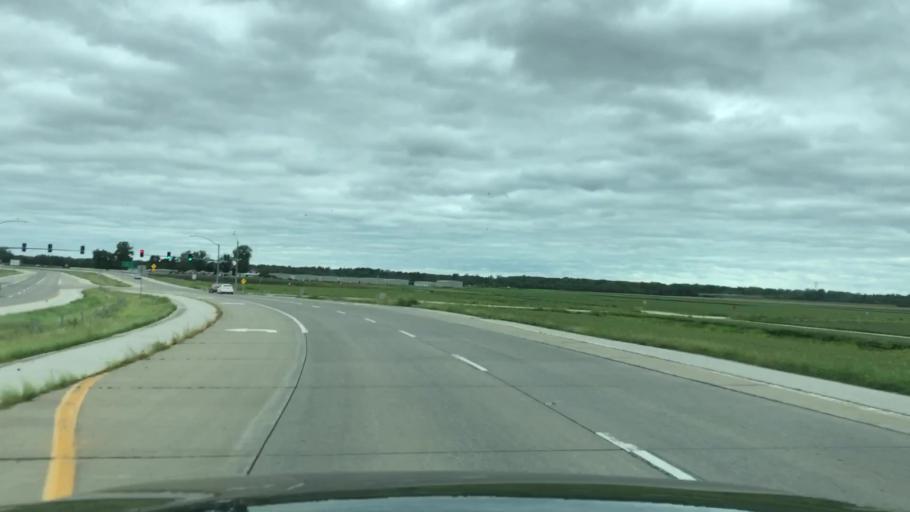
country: US
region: Missouri
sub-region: Saint Charles County
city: Saint Charles
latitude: 38.7290
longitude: -90.4943
